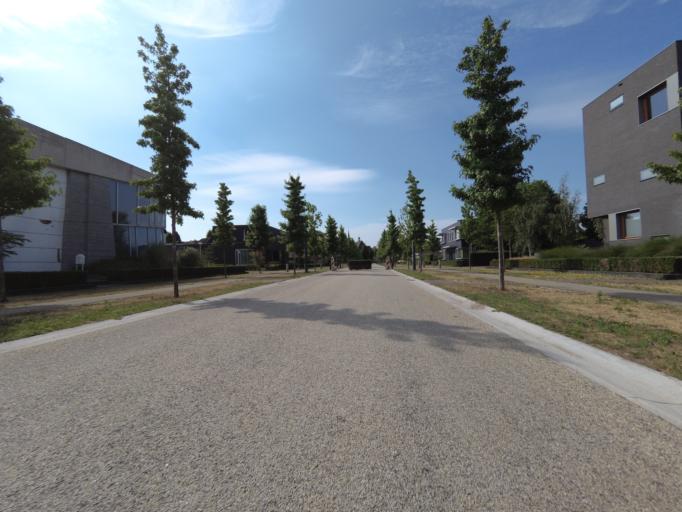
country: NL
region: Overijssel
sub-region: Gemeente Enschede
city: Enschede
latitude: 52.2296
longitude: 6.8959
